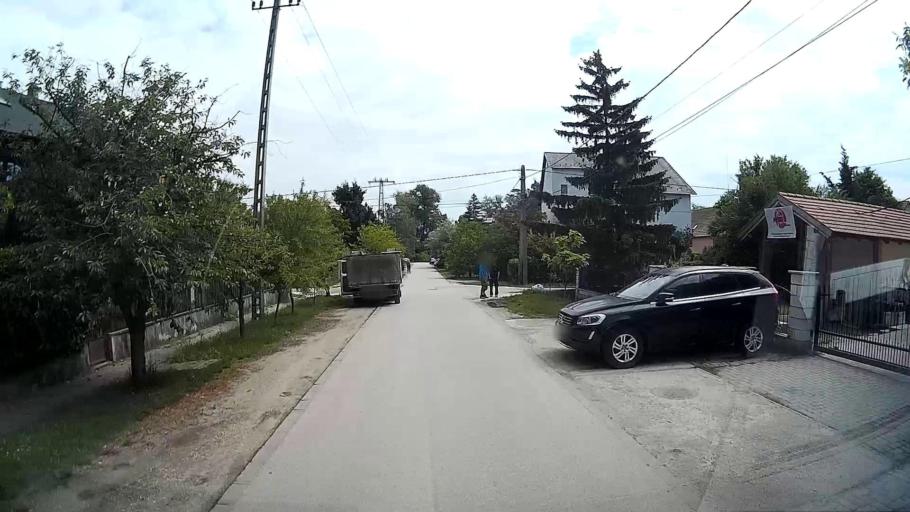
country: HU
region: Pest
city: Pomaz
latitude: 47.6448
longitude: 19.0383
